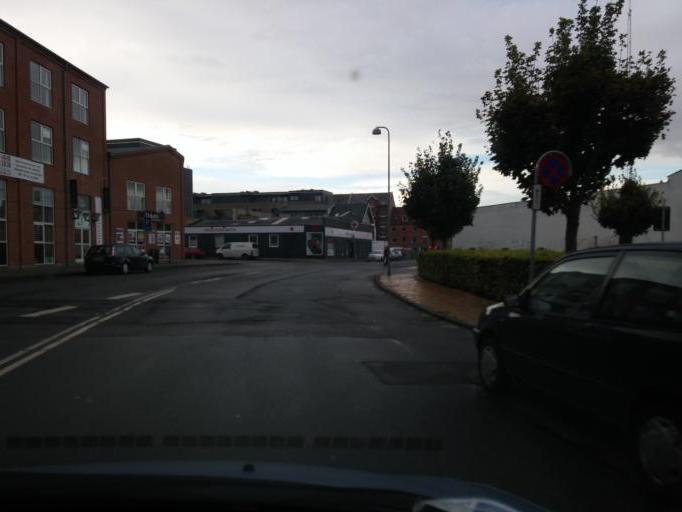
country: DK
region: South Denmark
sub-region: Odense Kommune
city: Odense
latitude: 55.3979
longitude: 10.3744
